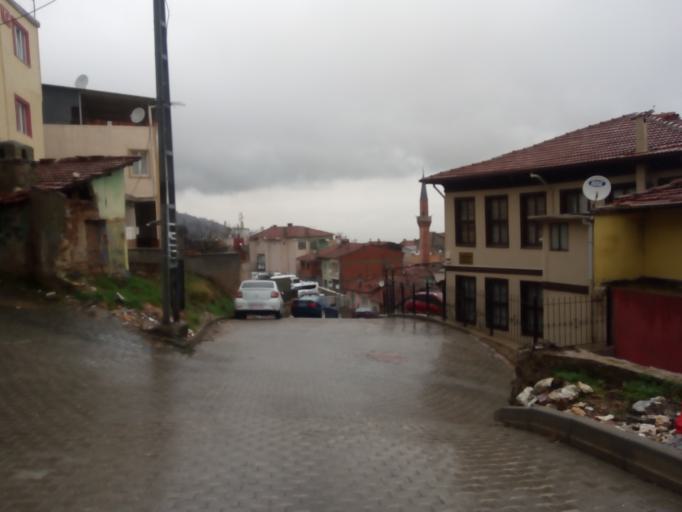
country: TR
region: Bursa
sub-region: Osmangazi
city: Bursa
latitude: 40.1778
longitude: 29.0578
